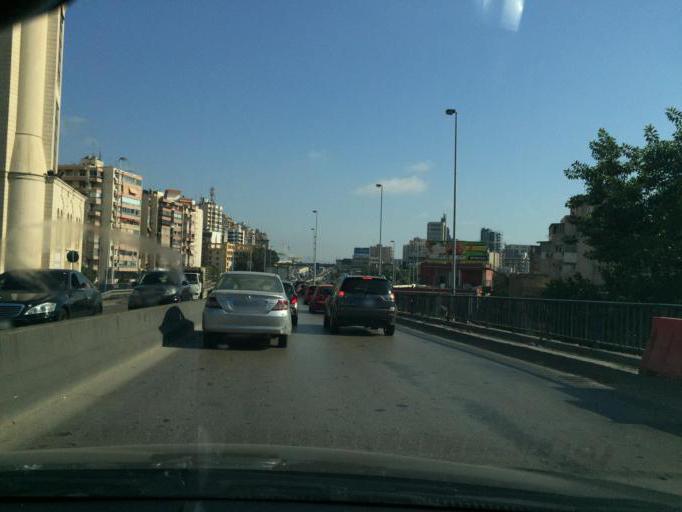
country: LB
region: Beyrouth
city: Beirut
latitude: 33.8778
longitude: 35.4952
